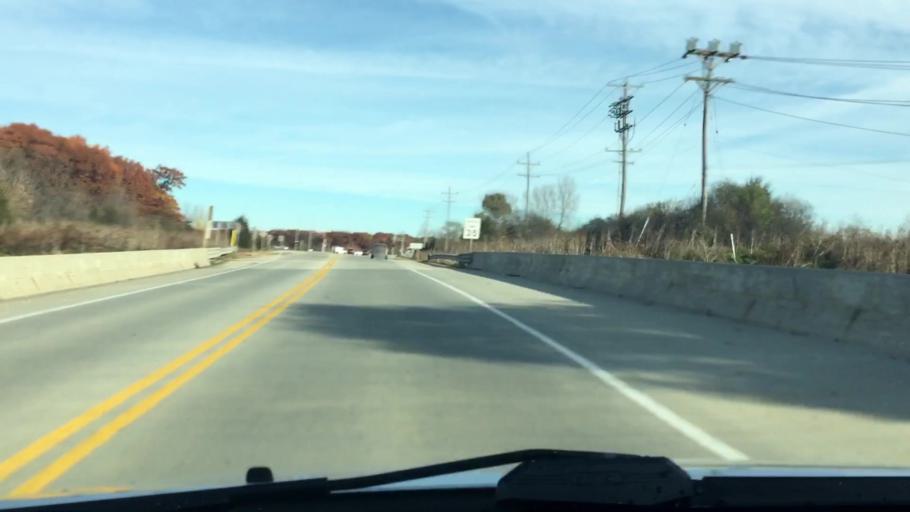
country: US
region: Wisconsin
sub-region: Waukesha County
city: Hartland
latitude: 43.1000
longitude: -88.3621
